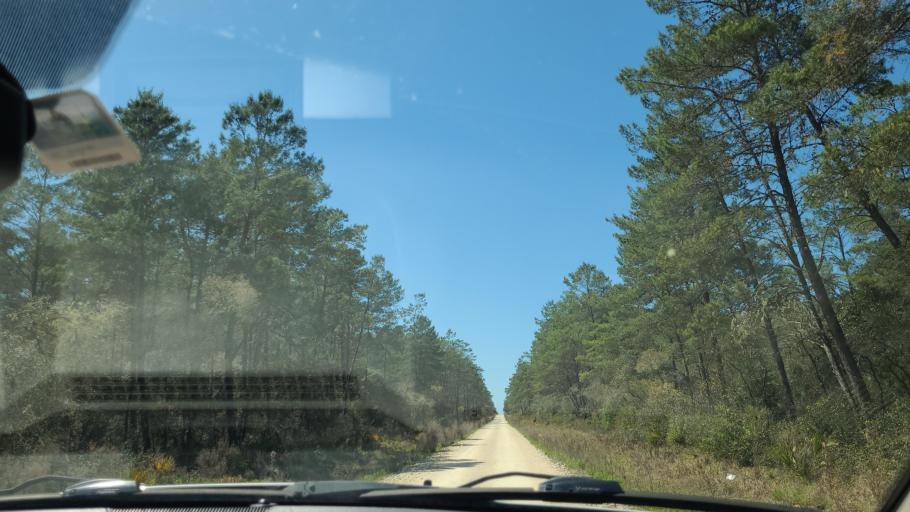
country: US
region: Florida
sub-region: Putnam County
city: Interlachen
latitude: 29.4284
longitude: -81.8753
